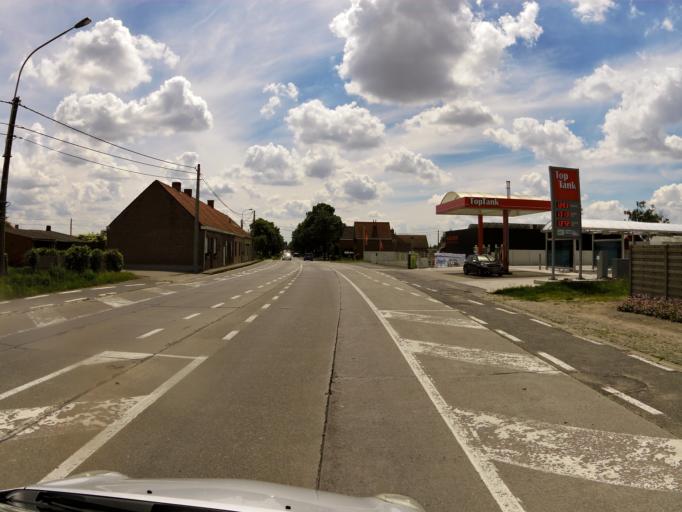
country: BE
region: Flanders
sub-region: Provincie West-Vlaanderen
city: Zonnebeke
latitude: 50.8985
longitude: 2.9395
